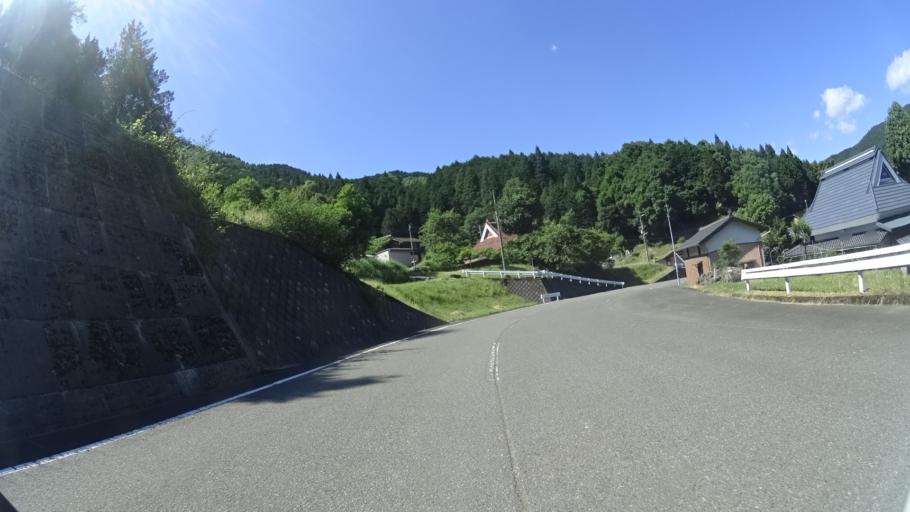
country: JP
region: Kyoto
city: Fukuchiyama
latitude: 35.4023
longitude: 135.0787
